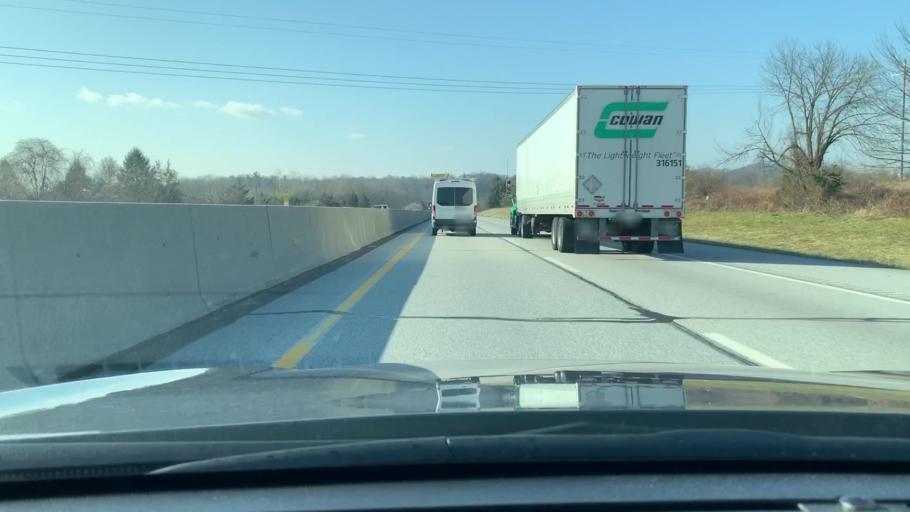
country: US
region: Pennsylvania
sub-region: Lancaster County
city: Elizabethtown
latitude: 40.2078
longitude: -76.6335
